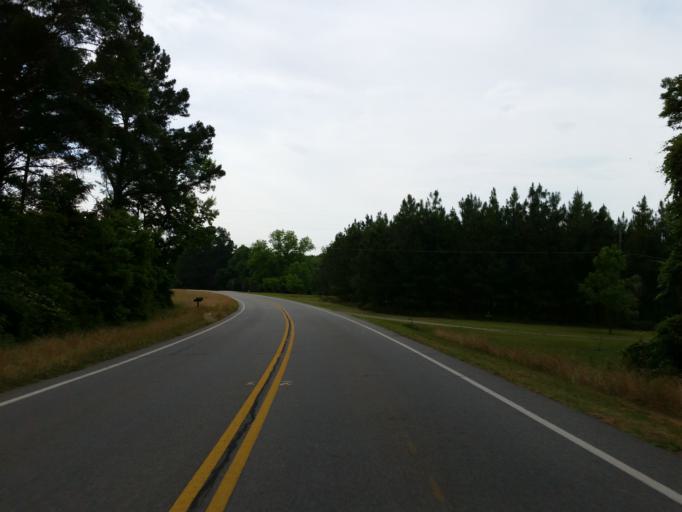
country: US
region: Georgia
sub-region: Dooly County
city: Vienna
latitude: 32.1334
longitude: -83.7956
